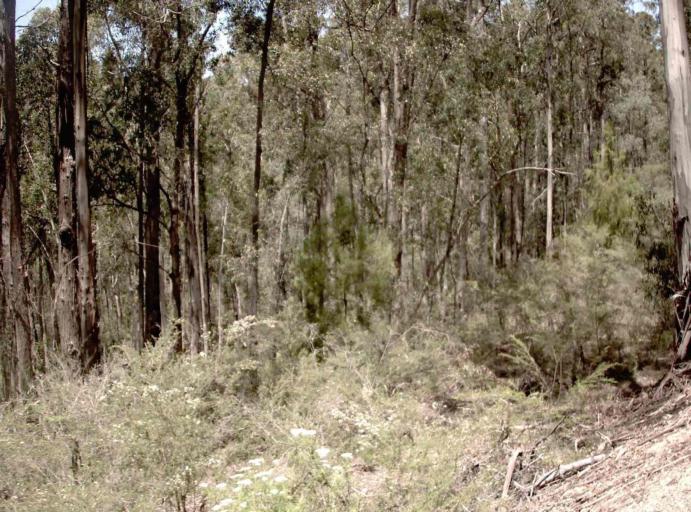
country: AU
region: Victoria
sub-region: East Gippsland
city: Lakes Entrance
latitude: -37.5989
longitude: 147.8890
